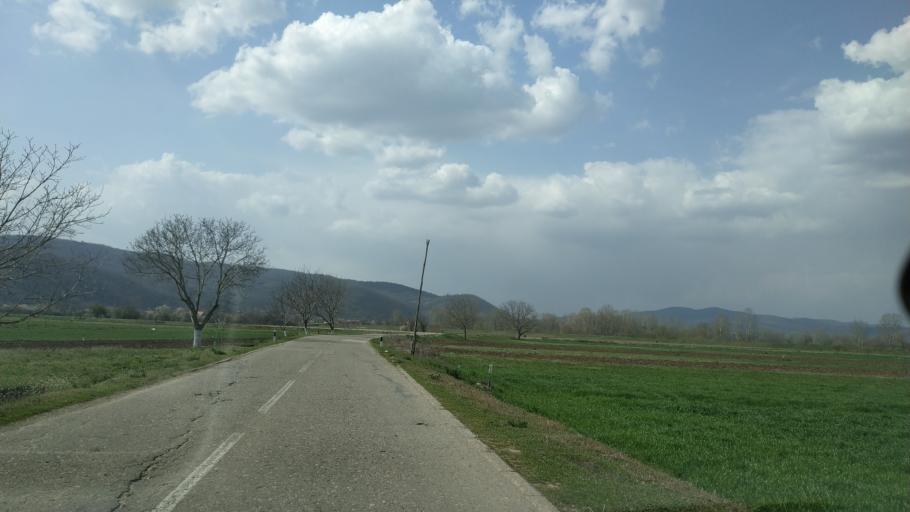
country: RS
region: Central Serbia
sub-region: Nisavski Okrug
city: Razanj
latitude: 43.5882
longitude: 21.5677
